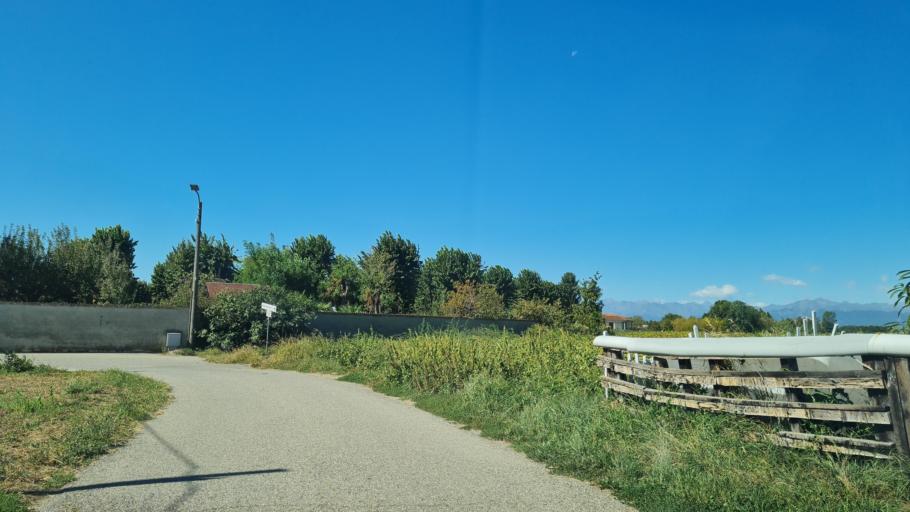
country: IT
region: Piedmont
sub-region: Provincia di Novara
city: Sillavengo
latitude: 45.5222
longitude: 8.4432
